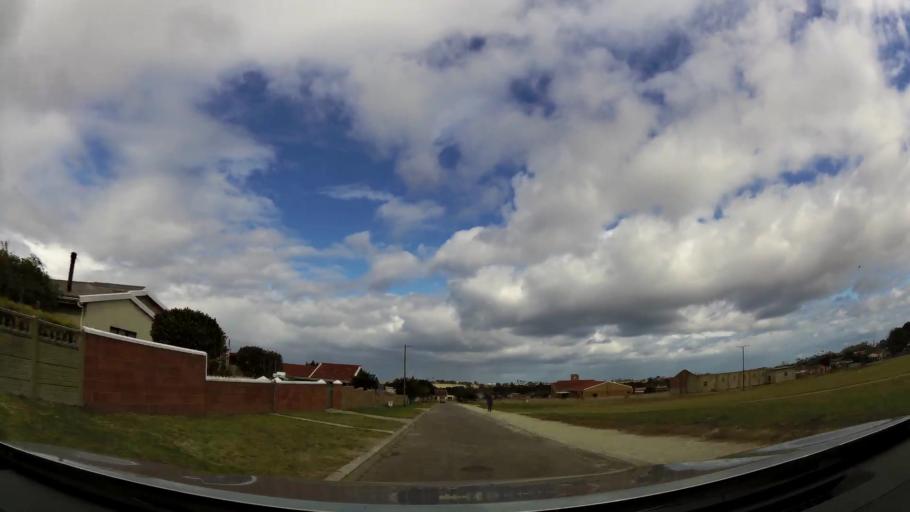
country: ZA
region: Western Cape
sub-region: Eden District Municipality
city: George
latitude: -34.0202
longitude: 22.4673
